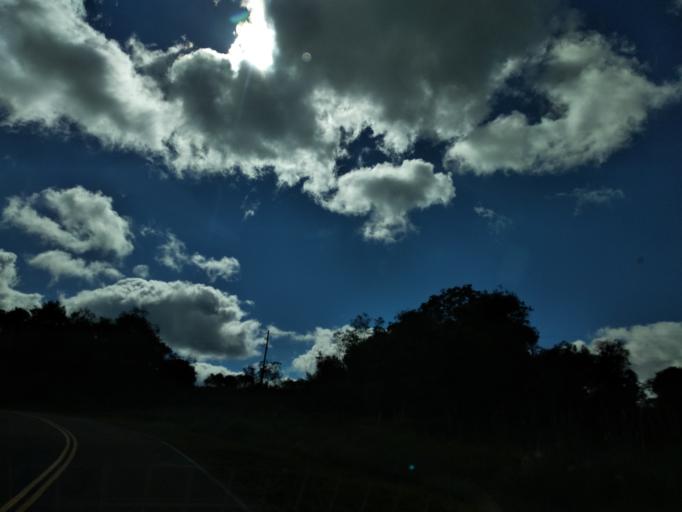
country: AR
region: Misiones
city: Santa Ana
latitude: -27.4226
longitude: -55.5672
